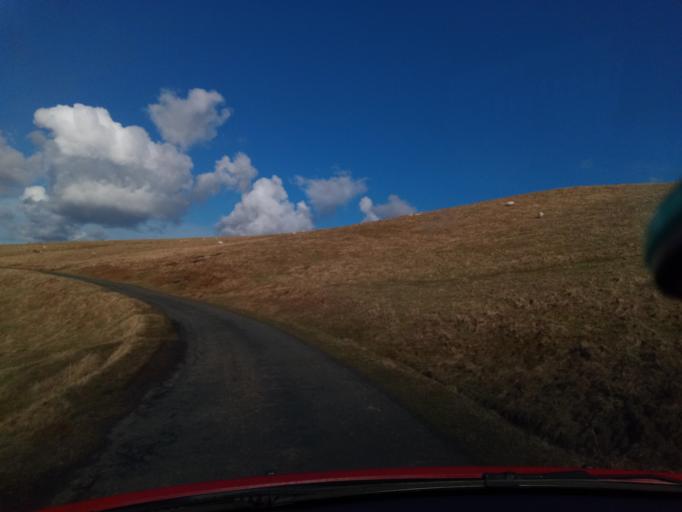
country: GB
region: Scotland
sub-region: The Scottish Borders
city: Hawick
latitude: 55.4545
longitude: -2.8795
